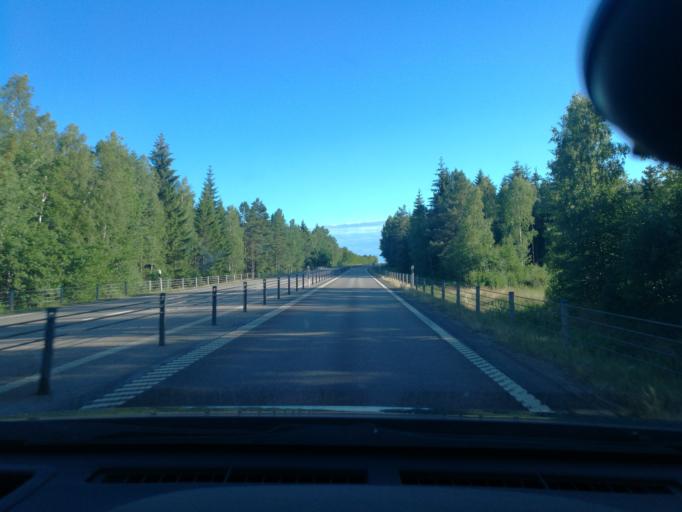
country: SE
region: Kalmar
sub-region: Monsteras Kommun
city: Timmernabben
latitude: 56.9928
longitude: 16.4118
